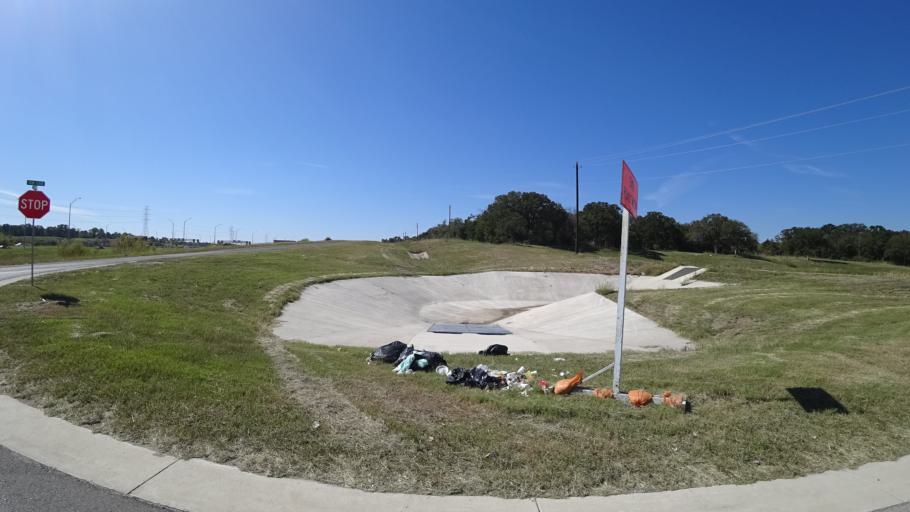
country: US
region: Texas
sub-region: Travis County
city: Hornsby Bend
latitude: 30.2726
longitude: -97.5940
